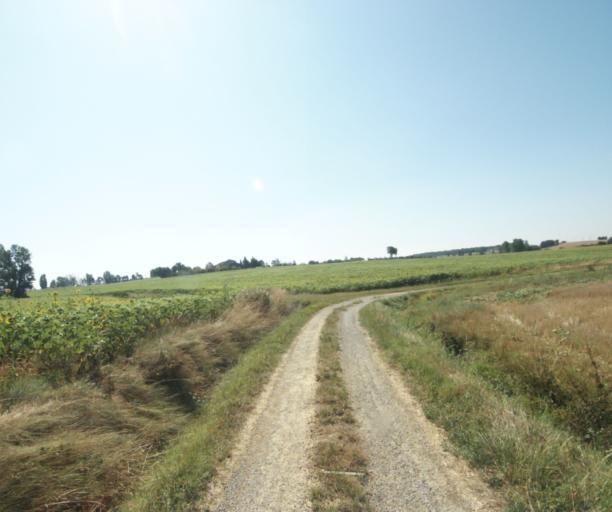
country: FR
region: Midi-Pyrenees
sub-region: Departement de la Haute-Garonne
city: Saint-Felix-Lauragais
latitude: 43.5119
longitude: 1.9189
